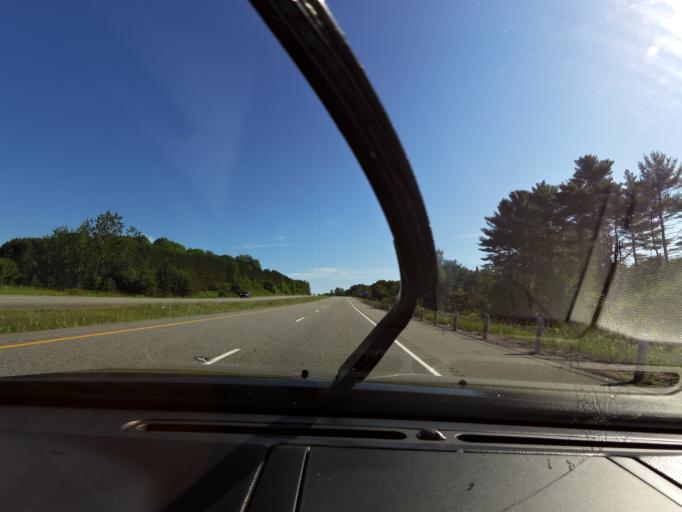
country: CA
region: Ontario
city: Bracebridge
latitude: 45.0387
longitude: -79.2909
